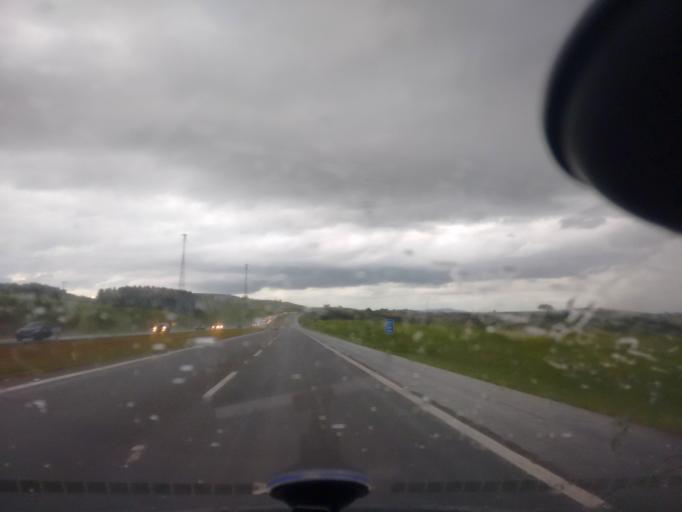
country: BR
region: Sao Paulo
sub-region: Santa Barbara D'Oeste
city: Santa Barbara d'Oeste
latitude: -22.6724
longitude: -47.4452
